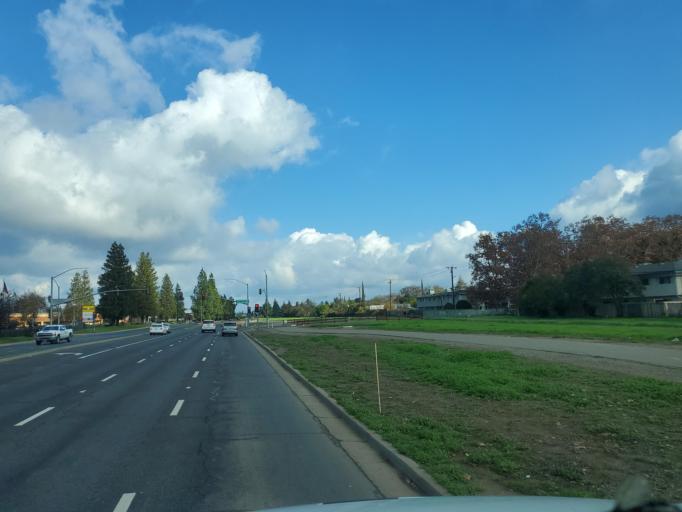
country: US
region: California
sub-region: San Joaquin County
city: Lincoln Village
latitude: 37.9970
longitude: -121.3043
